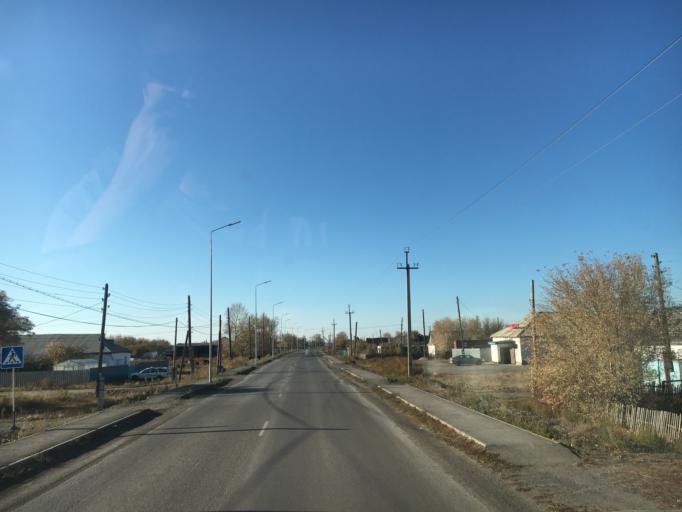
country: KZ
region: Qaraghandy
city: Tokarevka
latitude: 50.1370
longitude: 73.1798
